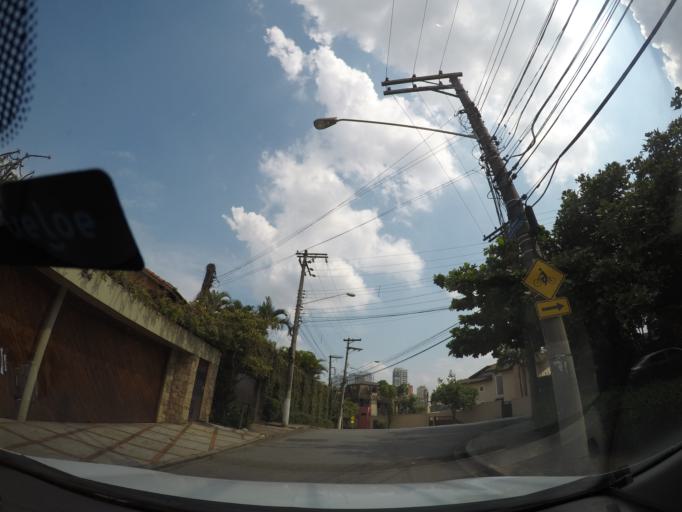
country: BR
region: Sao Paulo
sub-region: Sao Paulo
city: Sao Paulo
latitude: -23.6027
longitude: -46.7027
